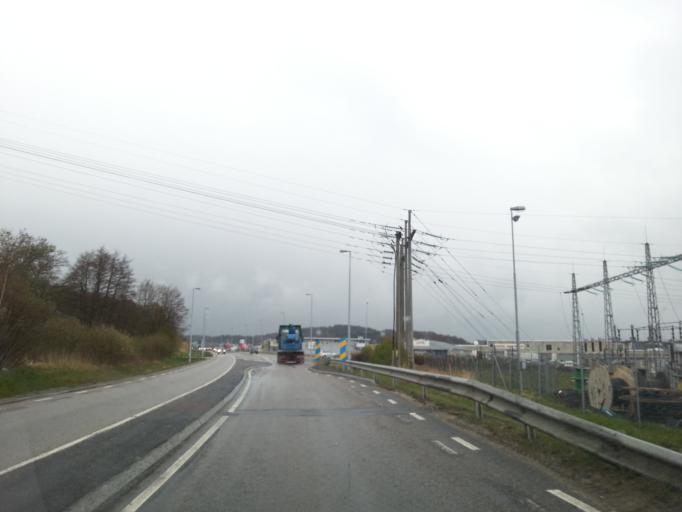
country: SE
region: Vaestra Goetaland
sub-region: Kungalvs Kommun
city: Kungalv
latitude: 57.8781
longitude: 11.9768
